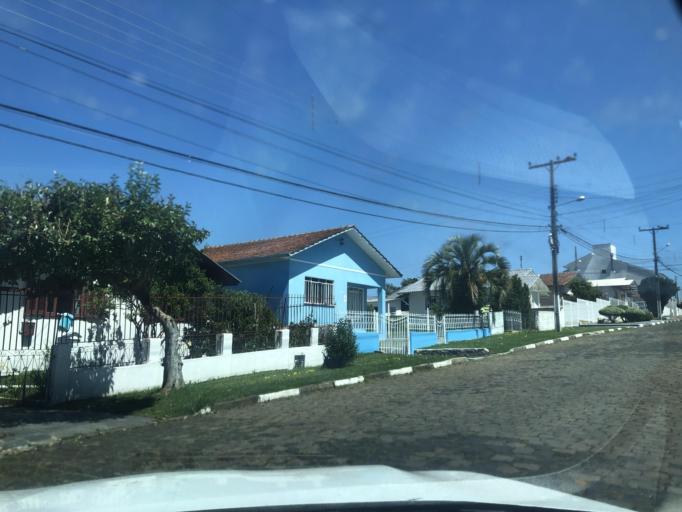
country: BR
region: Santa Catarina
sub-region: Lages
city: Lages
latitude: -27.8214
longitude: -50.3112
